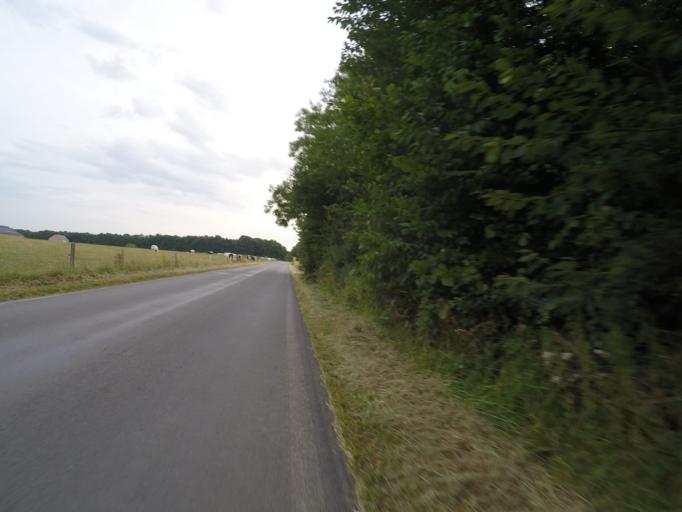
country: BE
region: Wallonia
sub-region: Province de Namur
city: Assesse
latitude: 50.3442
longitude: 5.0180
